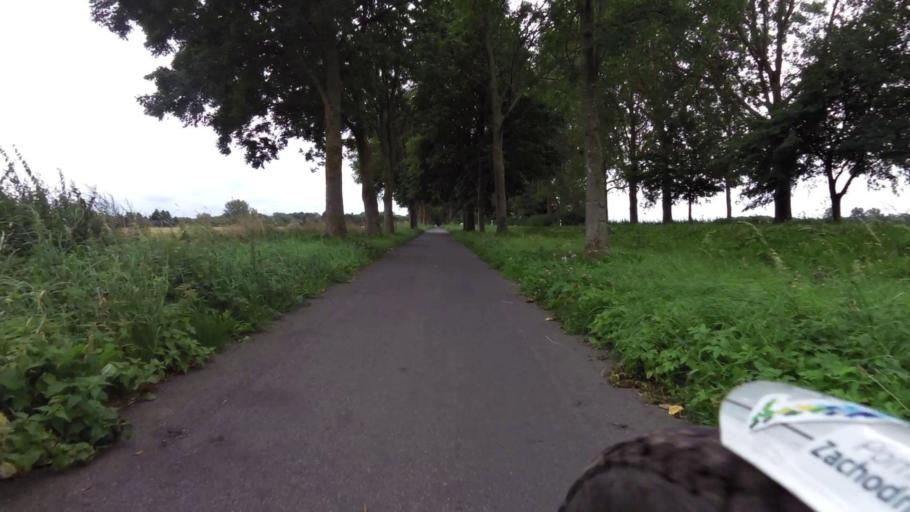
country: PL
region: West Pomeranian Voivodeship
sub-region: Powiat koszalinski
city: Mielno
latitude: 54.2270
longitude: 16.0761
